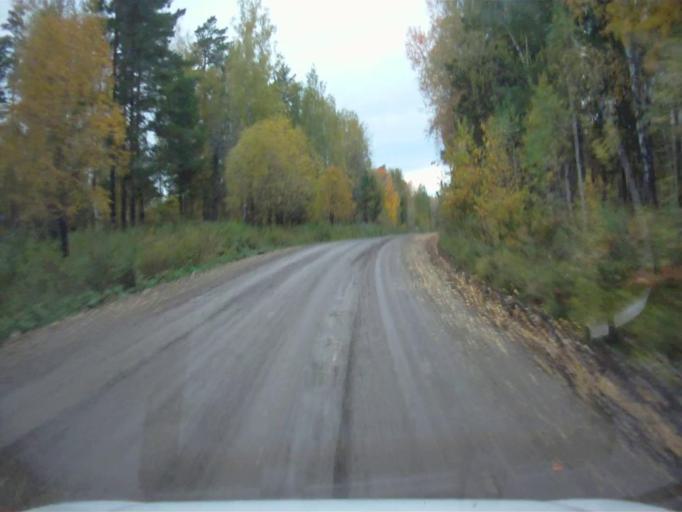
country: RU
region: Chelyabinsk
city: Nyazepetrovsk
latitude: 56.1120
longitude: 59.3703
